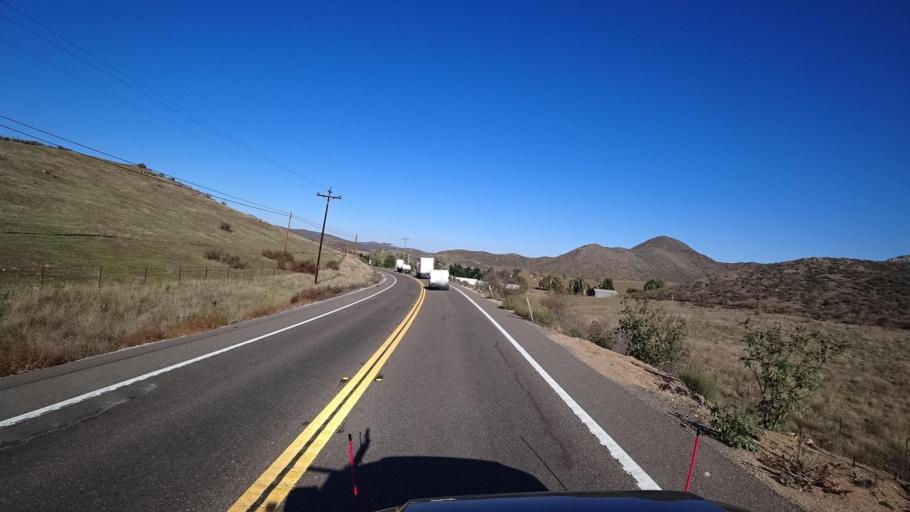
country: US
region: California
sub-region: San Diego County
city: Jamul
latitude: 32.6827
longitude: -116.8415
